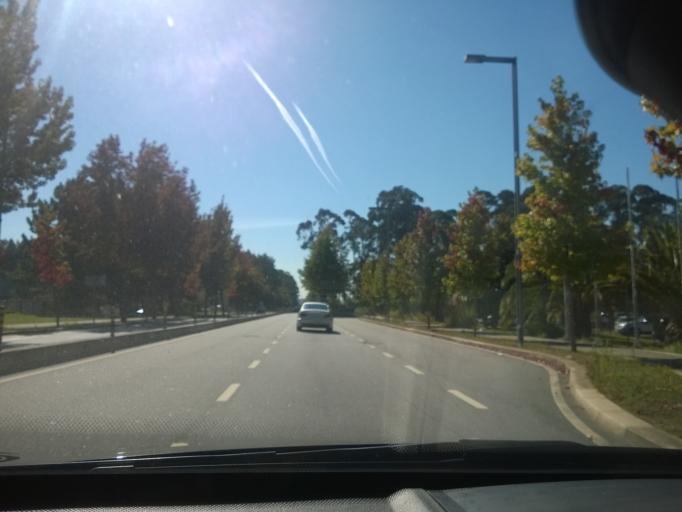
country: PT
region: Porto
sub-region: Maia
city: Anta
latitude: 41.2579
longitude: -8.6338
